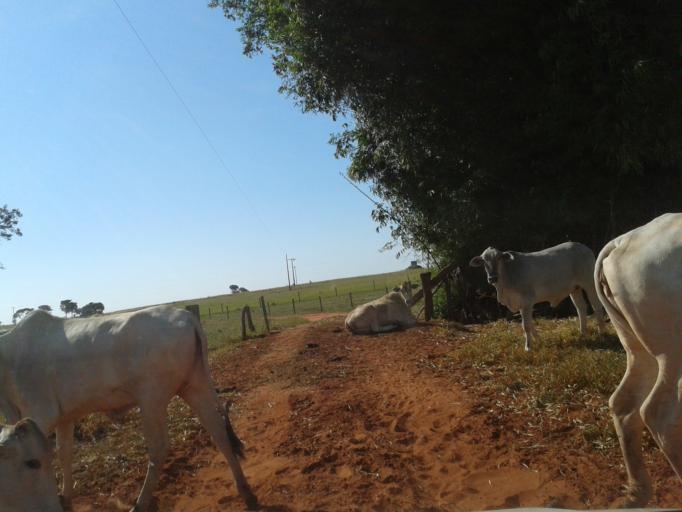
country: BR
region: Minas Gerais
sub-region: Campina Verde
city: Campina Verde
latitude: -19.4537
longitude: -49.6748
